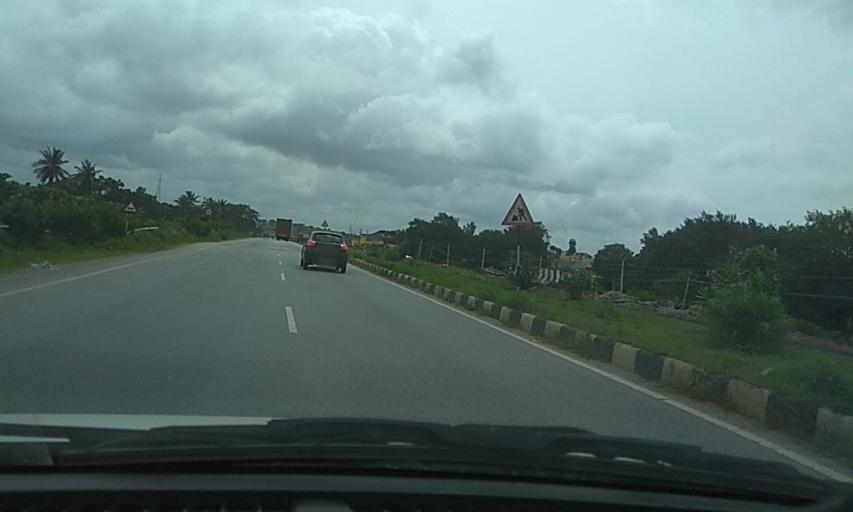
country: IN
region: Karnataka
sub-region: Davanagere
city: Mayakonda
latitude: 14.3666
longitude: 76.1553
